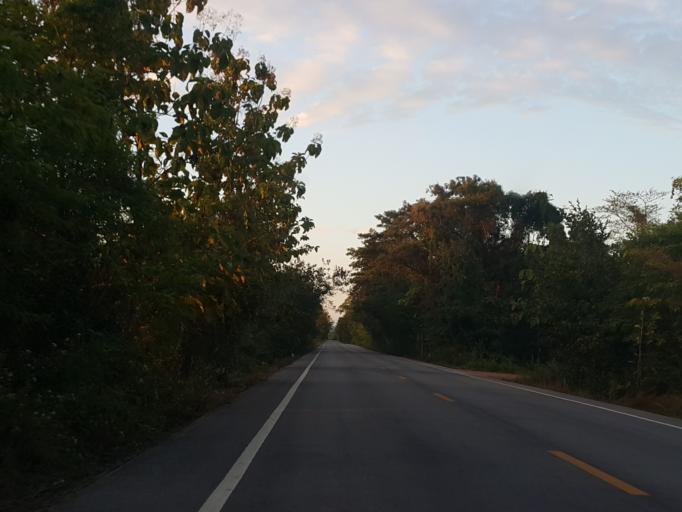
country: TH
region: Lampang
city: Mae Mo
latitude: 18.4362
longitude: 99.6405
